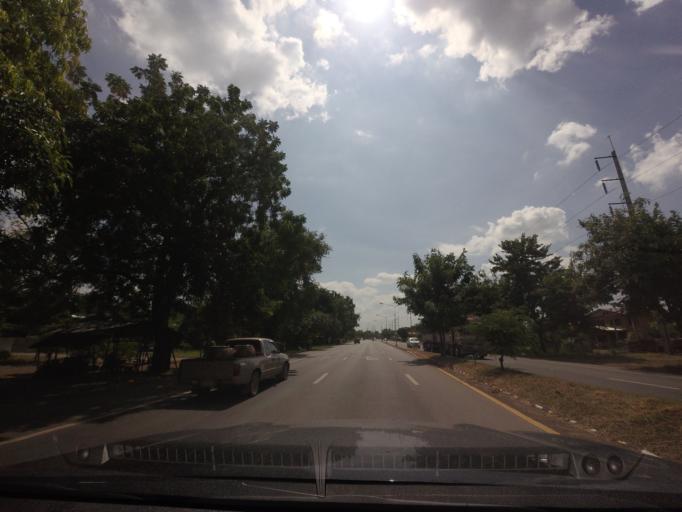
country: TH
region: Phetchabun
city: Nong Phai
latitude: 15.9438
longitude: 101.0319
